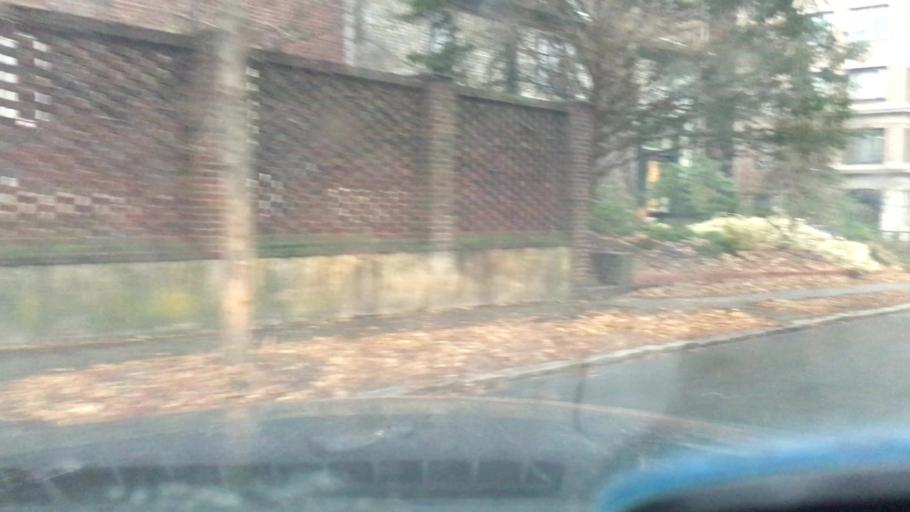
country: US
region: Massachusetts
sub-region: Norfolk County
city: Brookline
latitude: 42.3442
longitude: -71.1106
